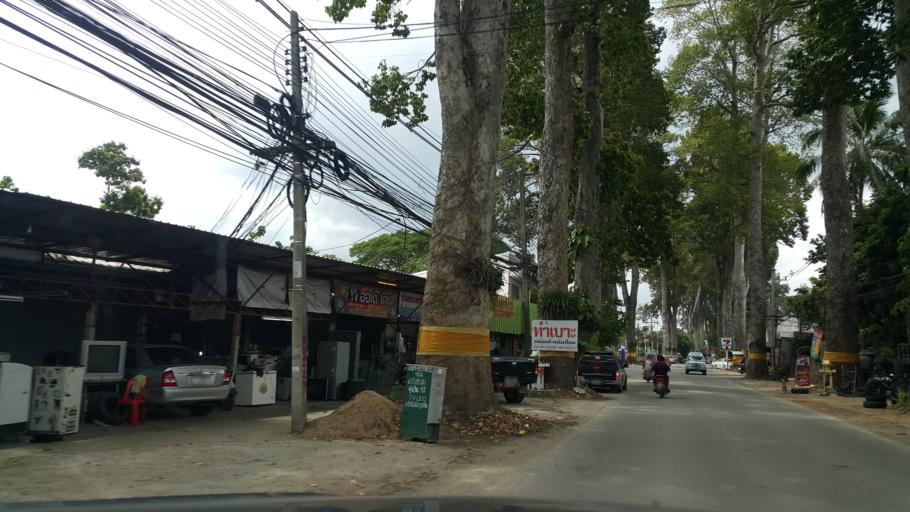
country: TH
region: Chiang Mai
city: Saraphi
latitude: 18.7359
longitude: 99.0161
